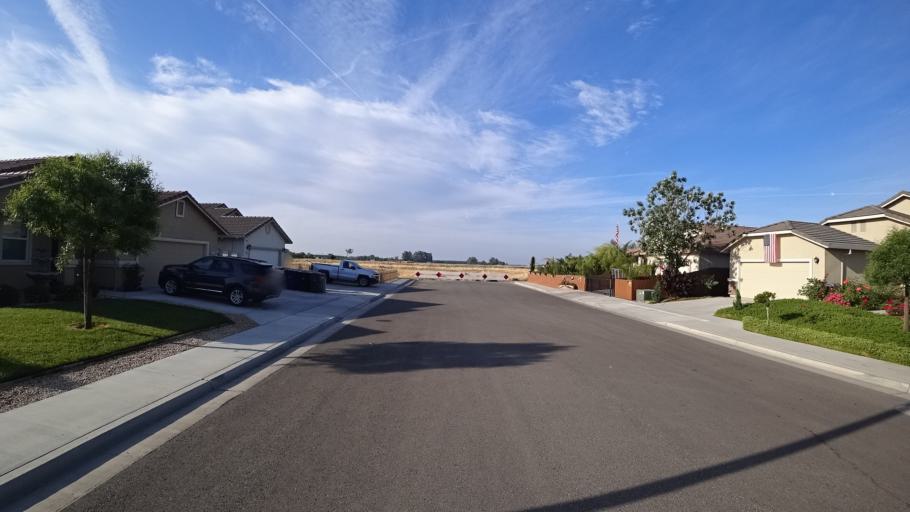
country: US
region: California
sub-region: Kings County
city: Armona
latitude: 36.3078
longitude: -119.6754
